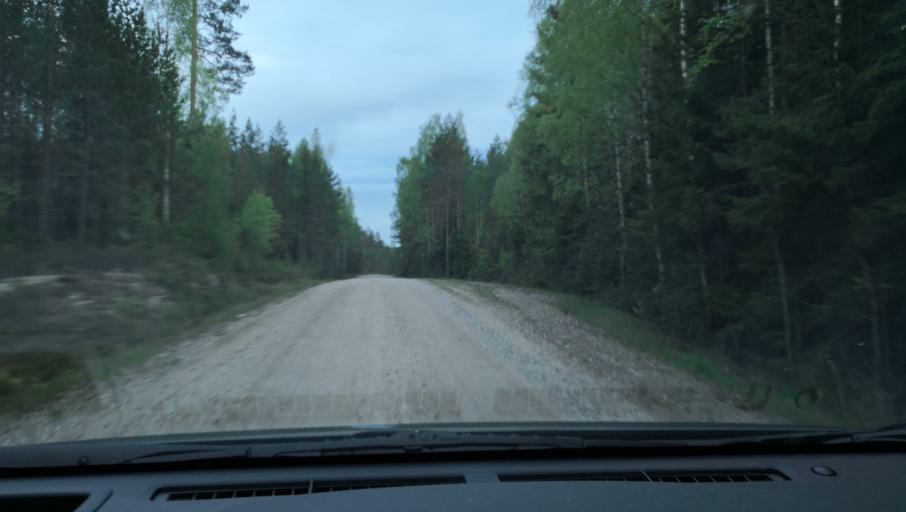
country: SE
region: Vaestmanland
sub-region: Skinnskattebergs Kommun
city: Skinnskatteberg
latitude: 59.7652
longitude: 15.4575
